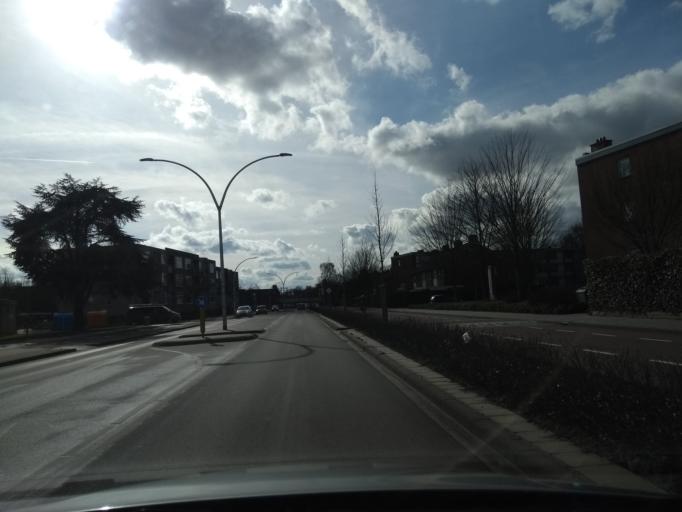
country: NL
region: Overijssel
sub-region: Gemeente Hengelo
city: Hengelo
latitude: 52.2711
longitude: 6.7811
